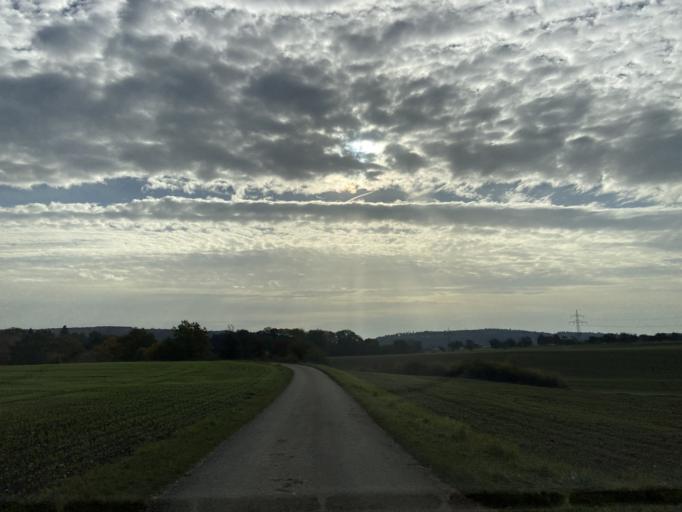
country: DE
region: Baden-Wuerttemberg
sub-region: Tuebingen Region
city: Bingen
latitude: 48.1194
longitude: 9.2754
